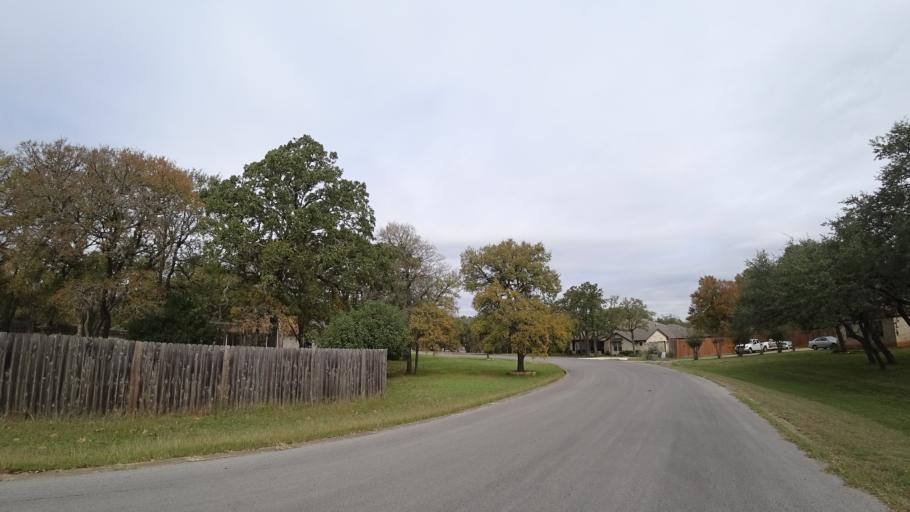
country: US
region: Texas
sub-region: Travis County
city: Shady Hollow
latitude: 30.1402
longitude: -97.8831
